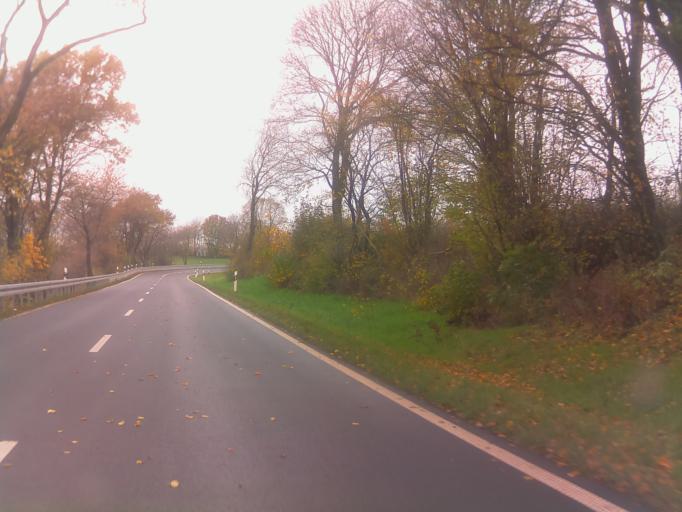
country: DE
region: Hesse
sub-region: Regierungsbezirk Giessen
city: Schotten
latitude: 50.4814
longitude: 9.1524
